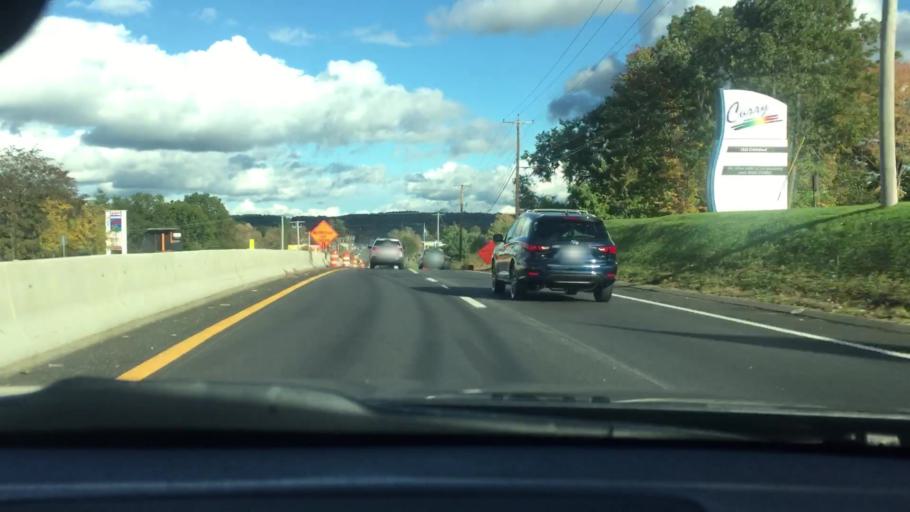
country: US
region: Massachusetts
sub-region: Worcester County
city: Westborough
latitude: 42.2844
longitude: -71.6211
